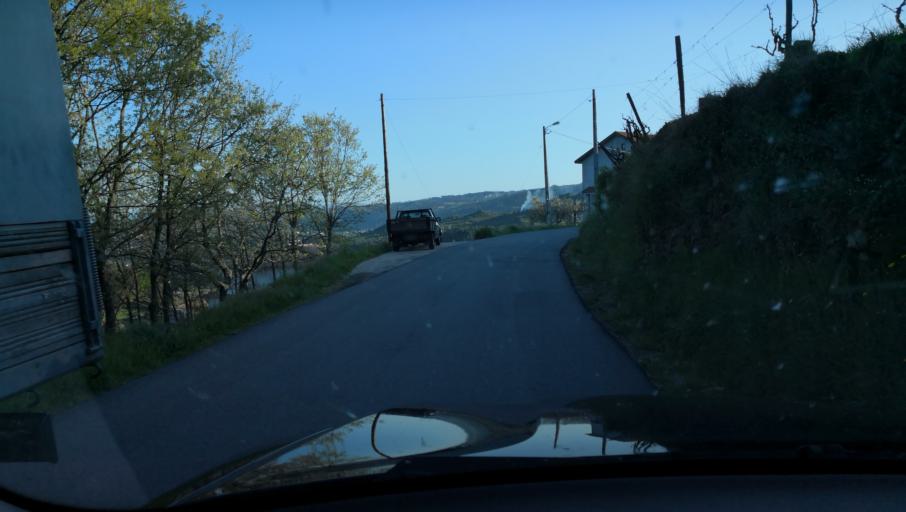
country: PT
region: Vila Real
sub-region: Vila Real
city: Vila Real
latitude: 41.3205
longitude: -7.7818
